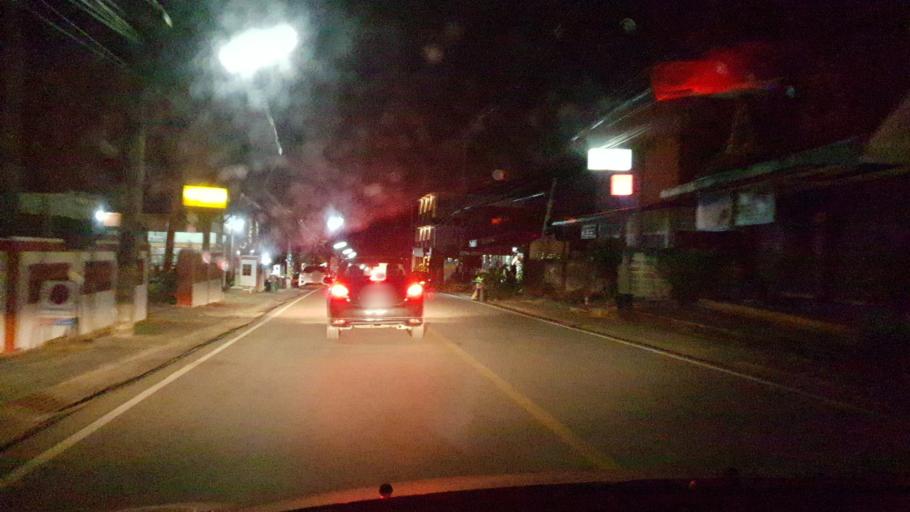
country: TH
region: Mae Hong Son
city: Khun Yuam
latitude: 18.8253
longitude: 97.9338
